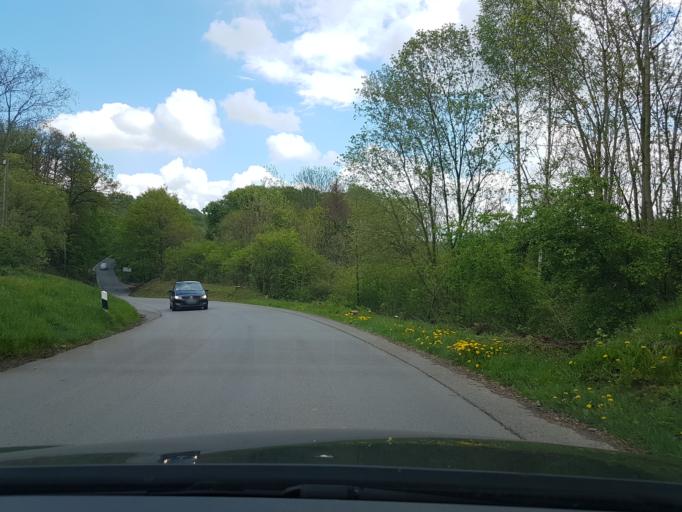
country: DE
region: Lower Saxony
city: Hameln
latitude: 52.1060
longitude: 9.4346
